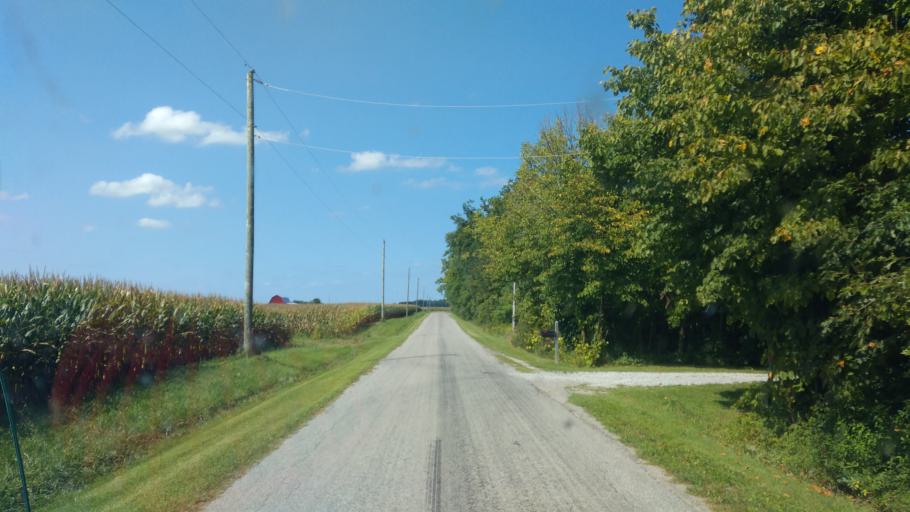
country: US
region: Ohio
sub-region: Union County
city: Richwood
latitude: 40.4993
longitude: -83.3957
